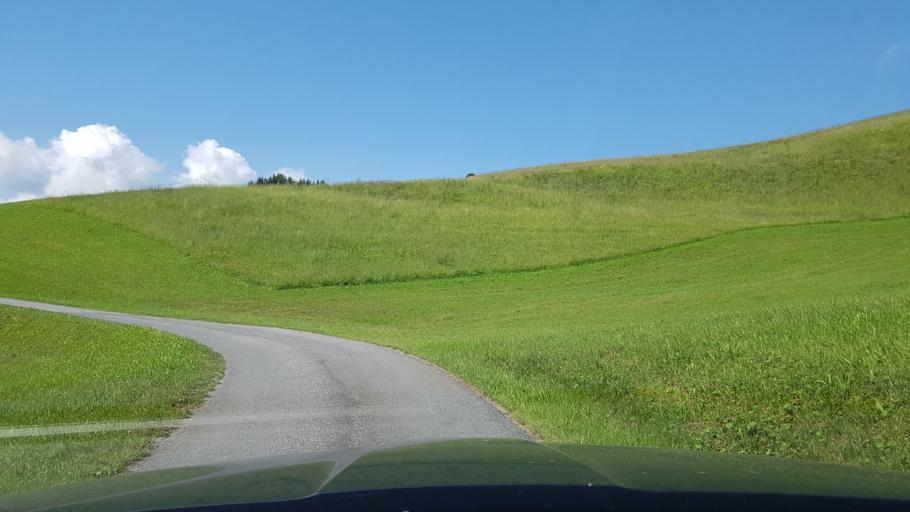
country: AT
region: Salzburg
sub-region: Politischer Bezirk Zell am See
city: Leogang
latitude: 47.4516
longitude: 12.7818
